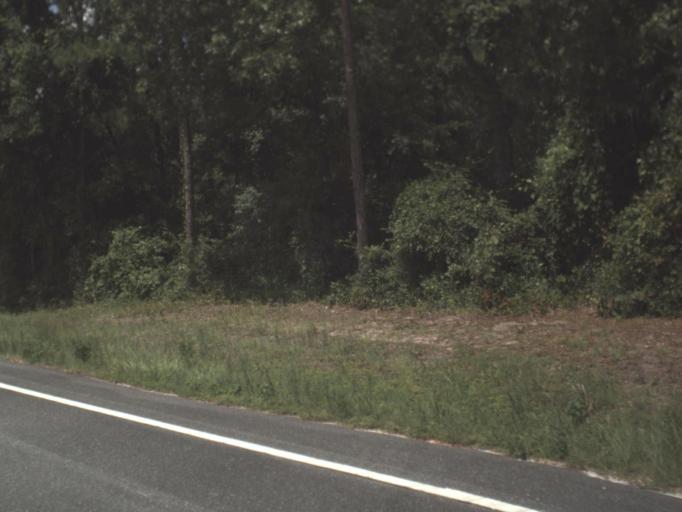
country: US
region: Florida
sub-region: Gilchrist County
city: Trenton
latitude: 29.8508
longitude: -82.8634
